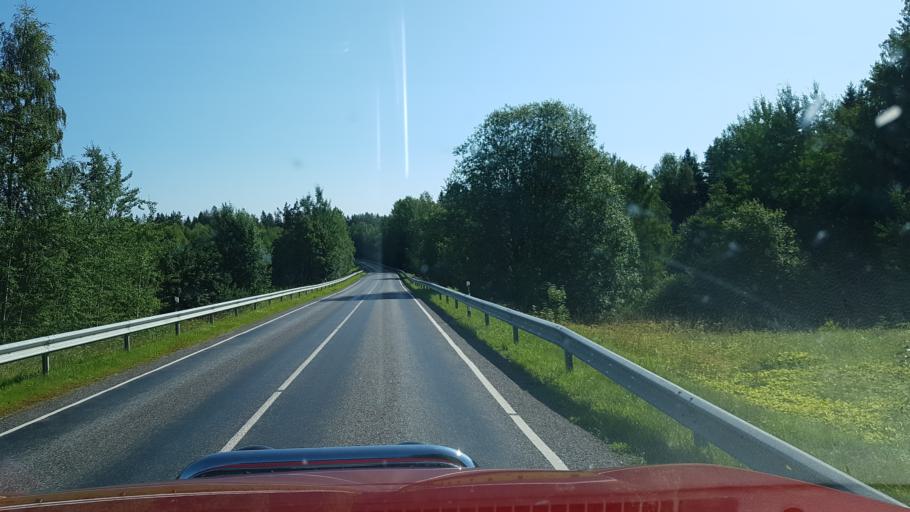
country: EE
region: Polvamaa
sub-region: Polva linn
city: Polva
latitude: 57.9877
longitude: 26.8911
